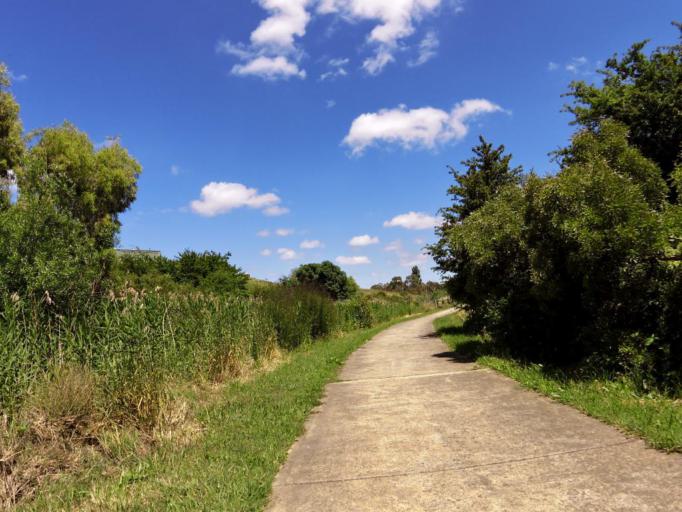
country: AU
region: Victoria
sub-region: Moreland
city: Fawkner
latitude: -37.7195
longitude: 144.9749
